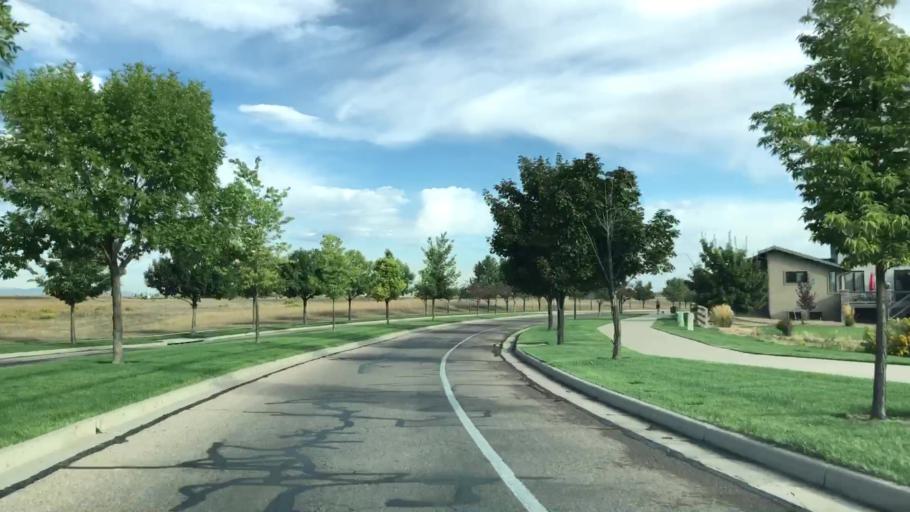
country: US
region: Colorado
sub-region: Weld County
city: Windsor
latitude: 40.4477
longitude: -104.9765
